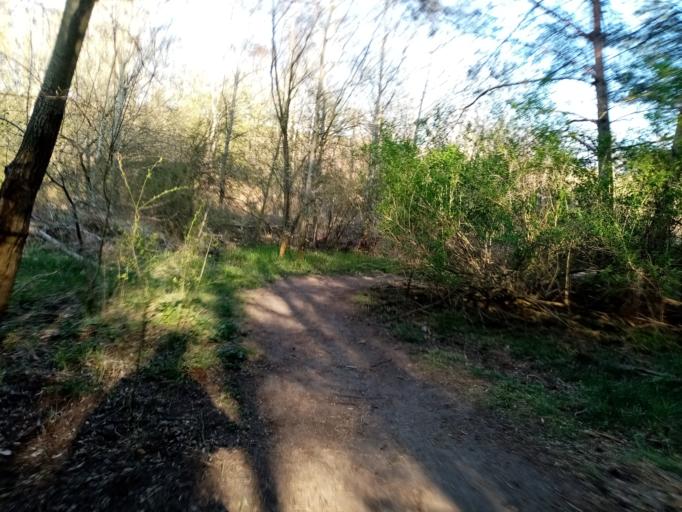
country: DE
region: Berlin
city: Karlshorst
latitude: 52.4726
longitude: 13.5391
